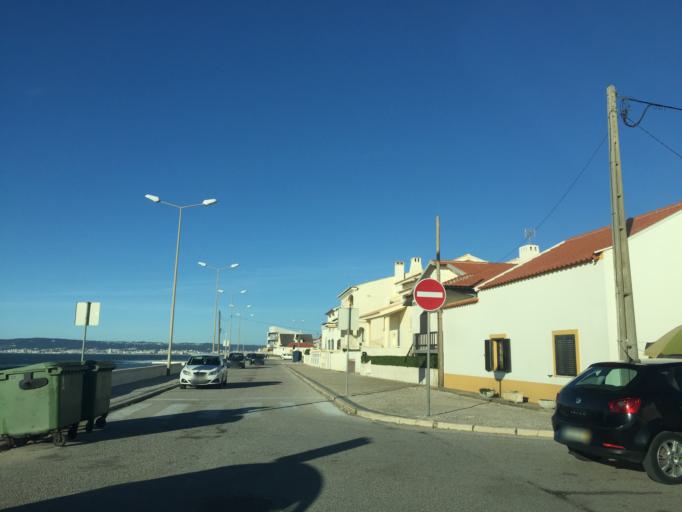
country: PT
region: Coimbra
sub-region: Figueira da Foz
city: Lavos
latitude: 40.0900
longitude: -8.8763
